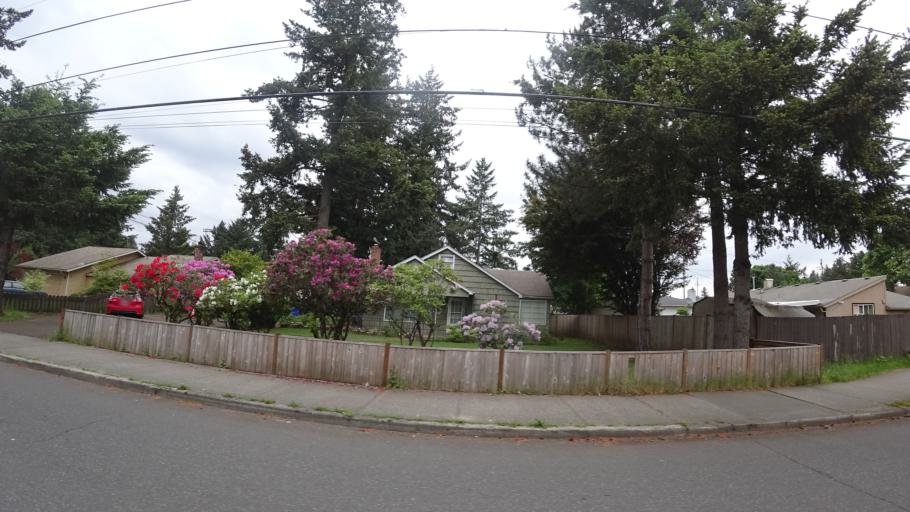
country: US
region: Oregon
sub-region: Multnomah County
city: Lents
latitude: 45.5117
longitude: -122.5248
